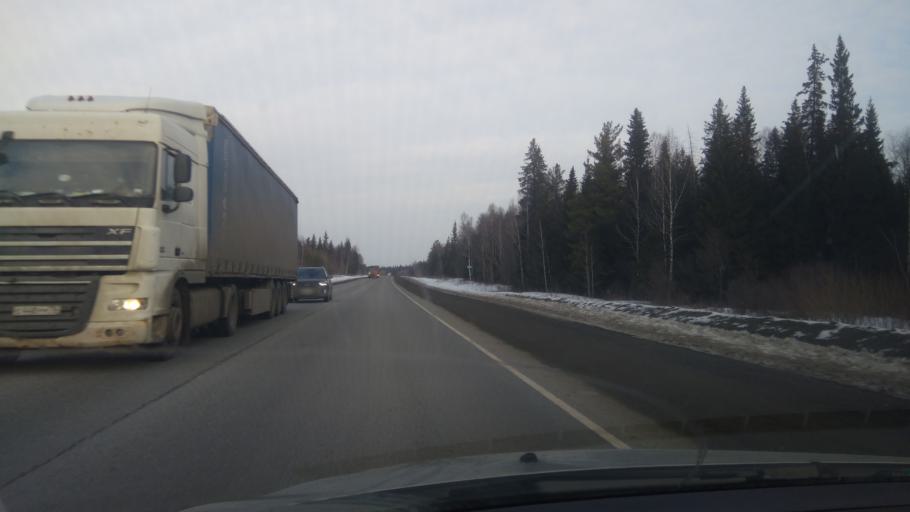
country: RU
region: Sverdlovsk
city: Atig
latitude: 56.8054
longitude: 59.3729
